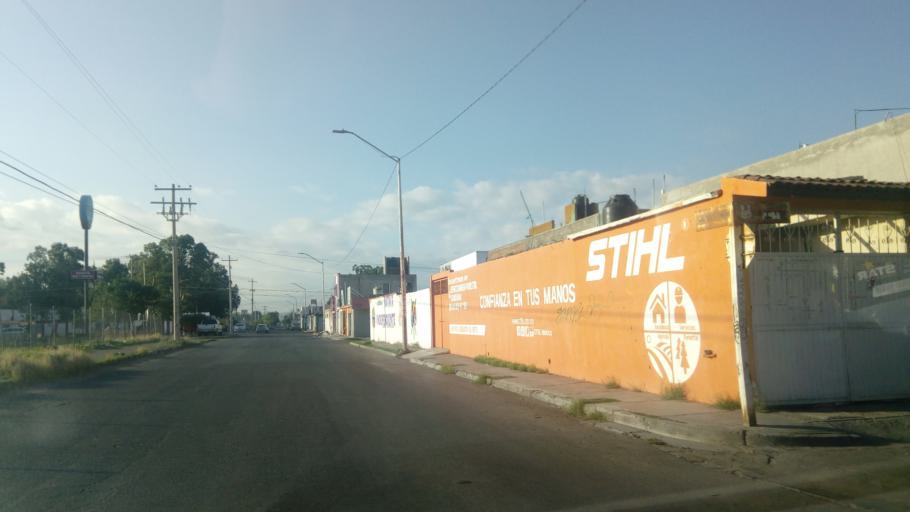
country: MX
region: Durango
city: Victoria de Durango
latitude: 24.0479
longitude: -104.6160
